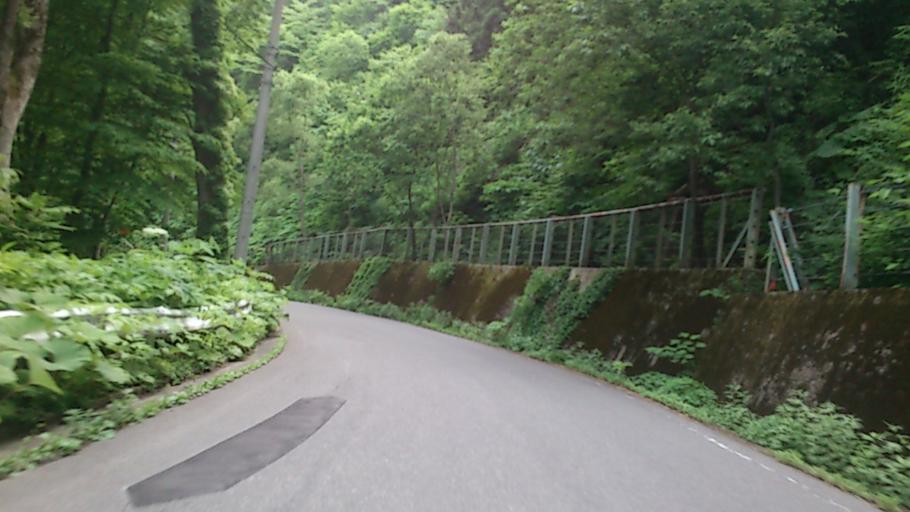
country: JP
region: Aomori
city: Hirosaki
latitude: 40.5170
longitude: 140.1797
